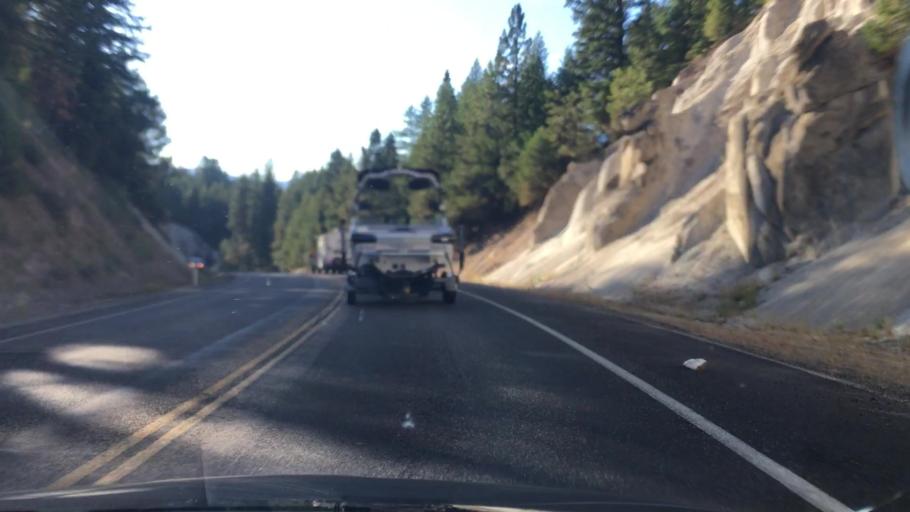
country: US
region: Idaho
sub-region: Valley County
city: Cascade
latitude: 44.5788
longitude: -116.0360
